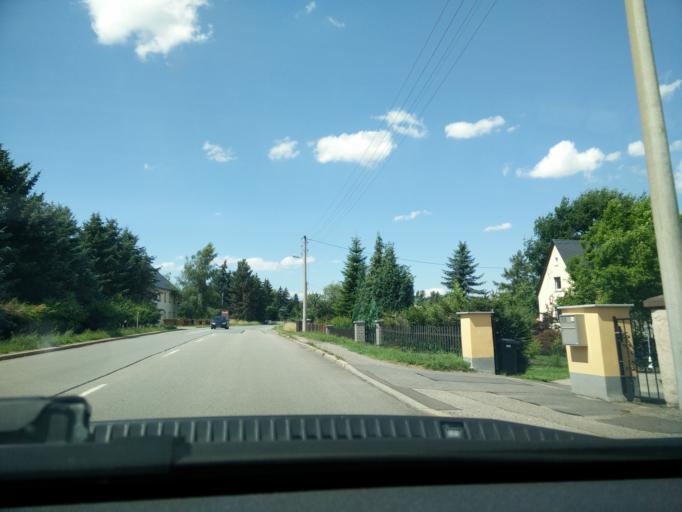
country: DE
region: Saxony
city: Muhlau
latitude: 50.9034
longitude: 12.7553
